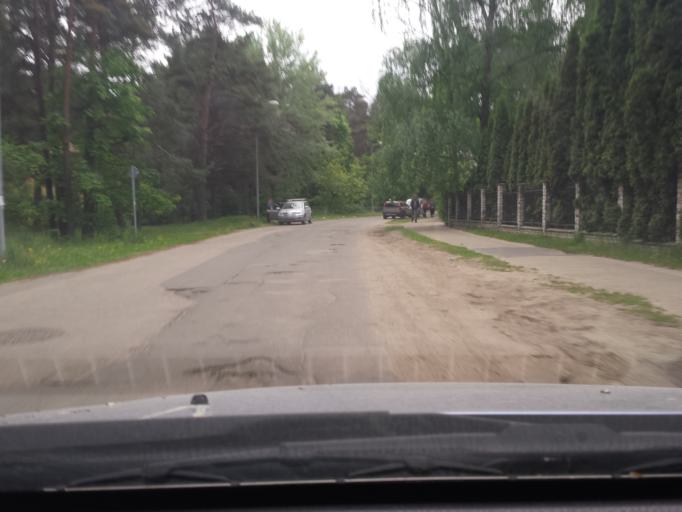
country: LV
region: Riga
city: Jaunciems
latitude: 57.0038
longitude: 24.1592
